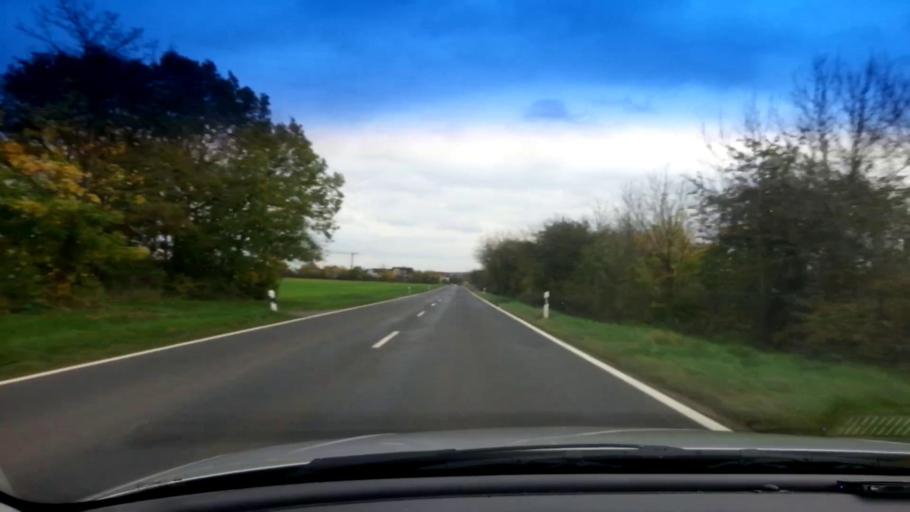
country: DE
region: Bavaria
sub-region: Regierungsbezirk Unterfranken
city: Stettfeld
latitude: 49.9503
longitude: 10.7433
